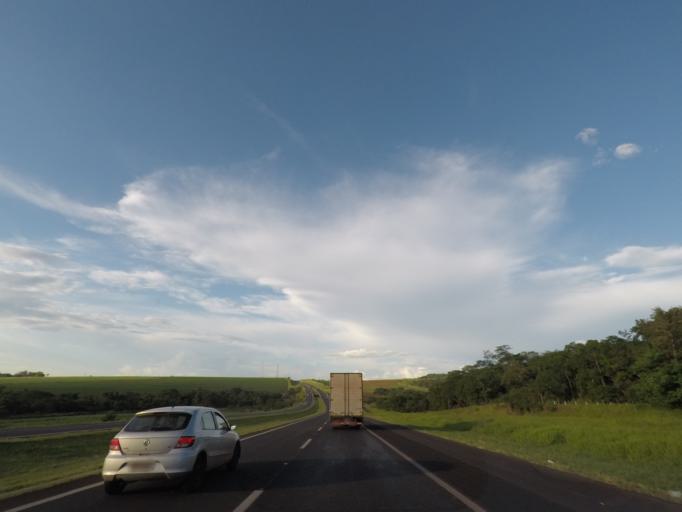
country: BR
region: Sao Paulo
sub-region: Ituverava
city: Ituverava
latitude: -20.2860
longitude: -47.7974
